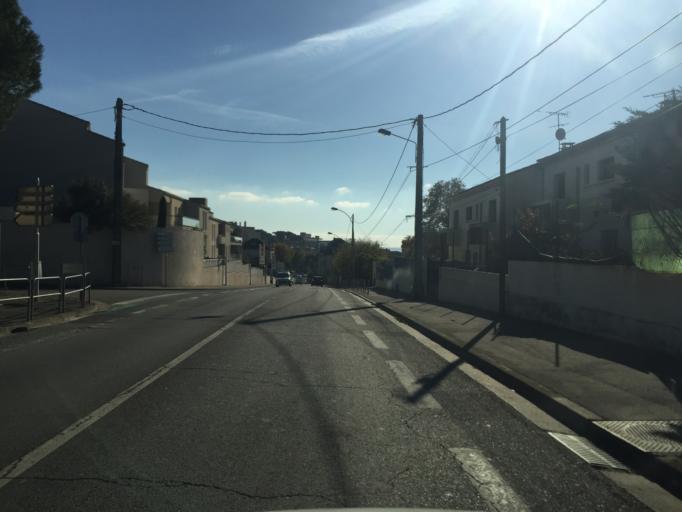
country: FR
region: Provence-Alpes-Cote d'Azur
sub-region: Departement des Bouches-du-Rhone
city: Salon-de-Provence
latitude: 43.6438
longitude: 5.1025
